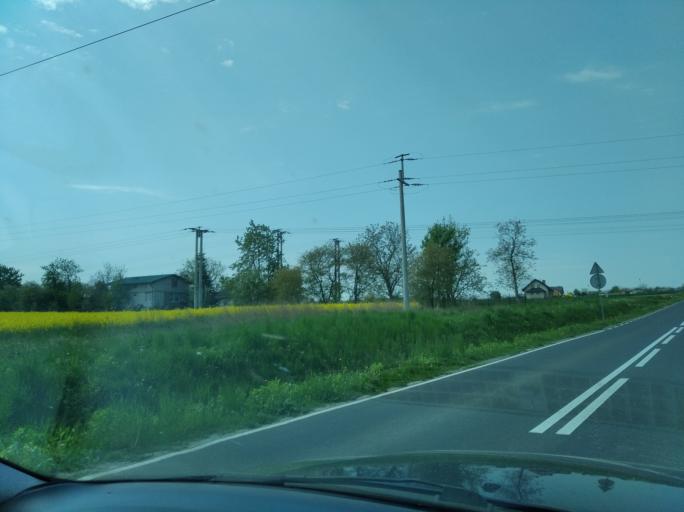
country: PL
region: Subcarpathian Voivodeship
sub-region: Powiat jaroslawski
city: Jaroslaw
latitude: 50.0000
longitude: 22.7047
